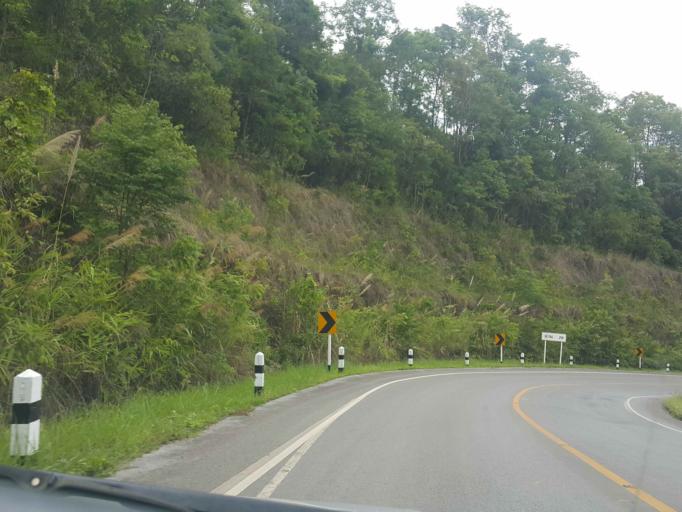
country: TH
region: Nan
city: Ban Luang
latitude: 18.8756
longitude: 100.5714
